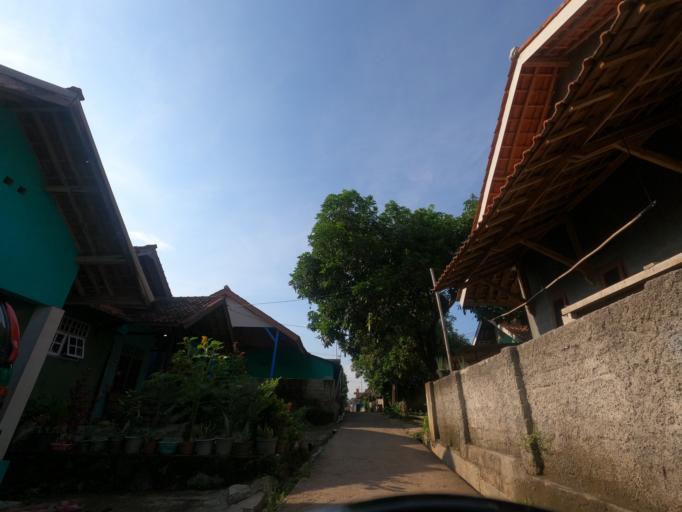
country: ID
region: West Java
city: Pamanukan
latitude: -6.5553
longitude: 107.8259
